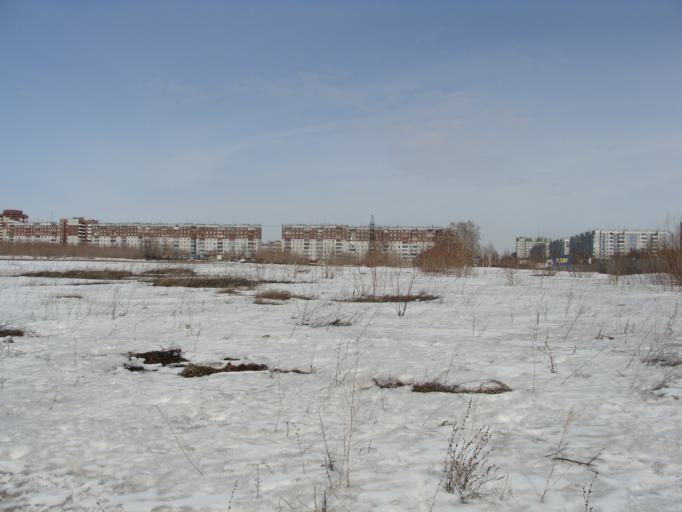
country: RU
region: Altai Krai
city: Novosilikatnyy
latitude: 53.3511
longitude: 83.6719
